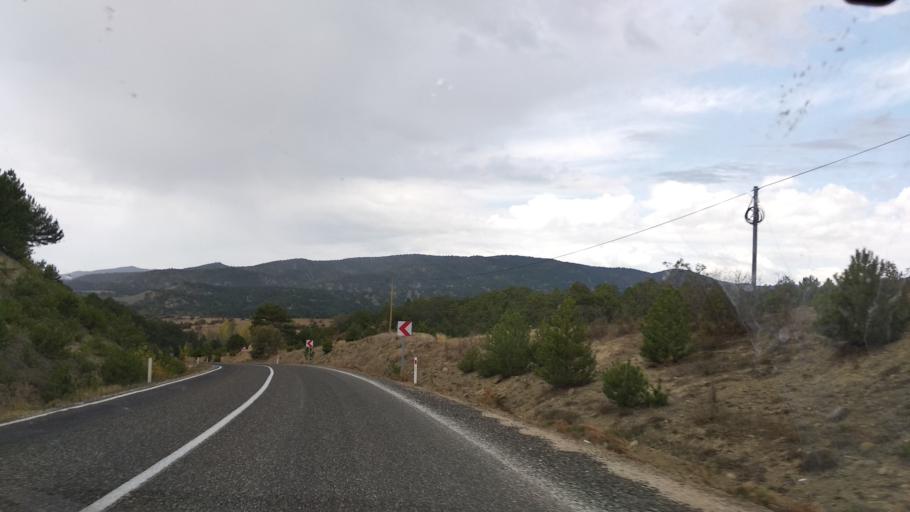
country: TR
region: Bolu
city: Seben
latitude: 40.3376
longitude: 31.4322
